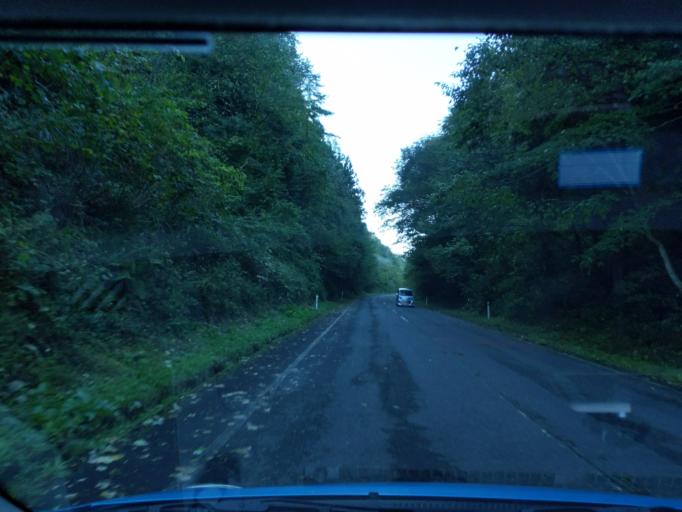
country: JP
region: Iwate
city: Ichinoseki
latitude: 39.0141
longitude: 141.0263
